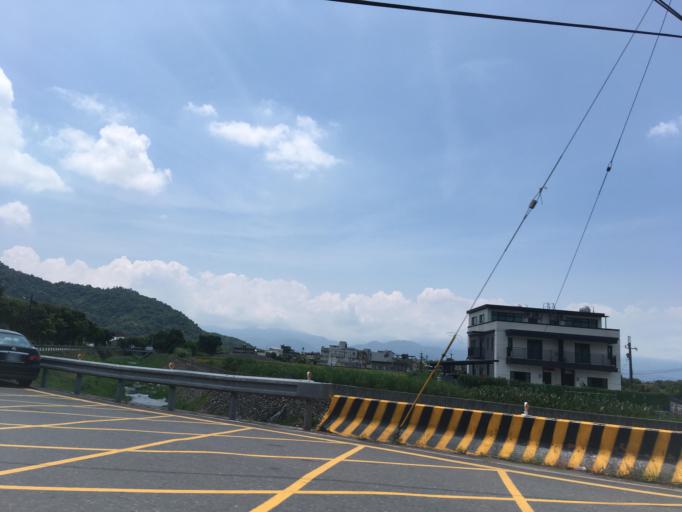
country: TW
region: Taiwan
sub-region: Yilan
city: Yilan
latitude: 24.6397
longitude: 121.7570
